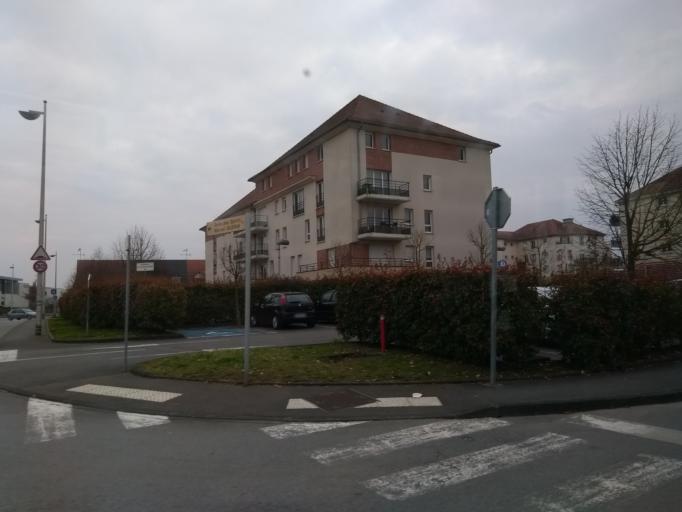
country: FR
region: Picardie
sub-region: Departement de l'Oise
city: Venette
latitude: 49.4212
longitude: 2.8104
